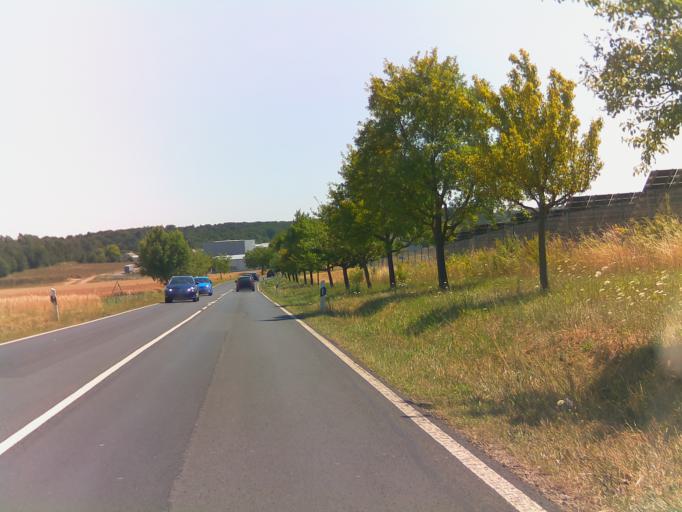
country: DE
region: Bavaria
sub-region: Regierungsbezirk Unterfranken
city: Gadheim
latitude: 49.8403
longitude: 9.9063
